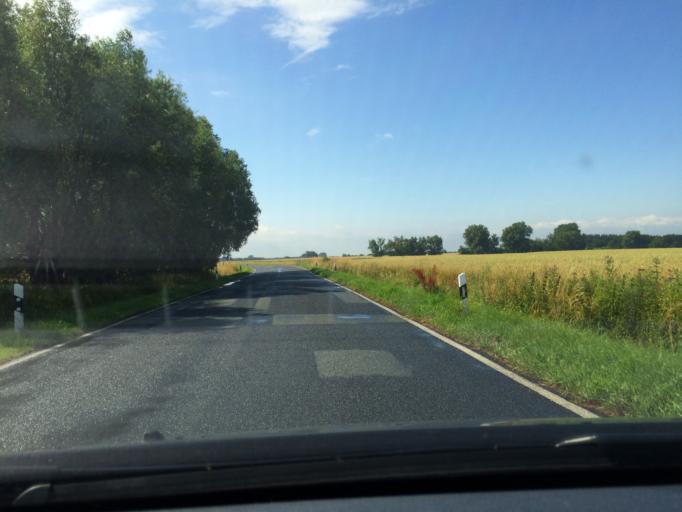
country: DE
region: Mecklenburg-Vorpommern
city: Altenpleen
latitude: 54.3835
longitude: 12.9432
